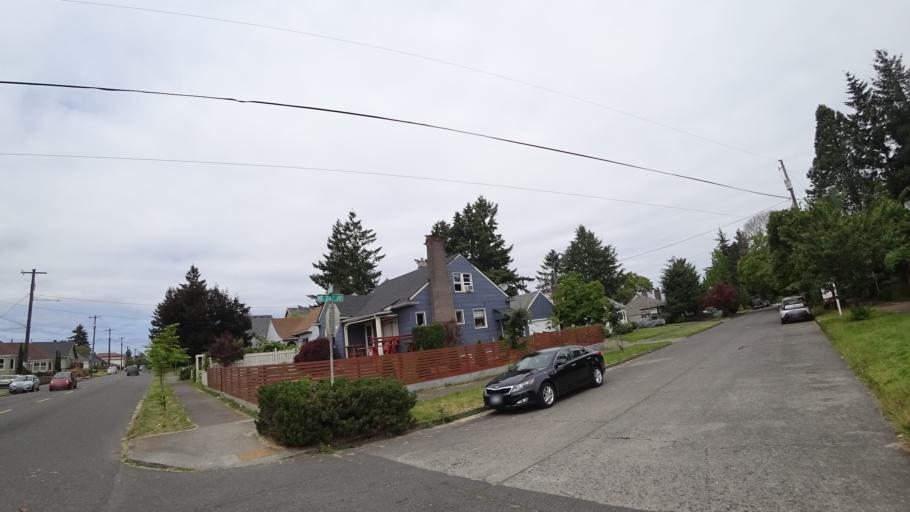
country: US
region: Oregon
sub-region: Multnomah County
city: Portland
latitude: 45.5627
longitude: -122.6393
